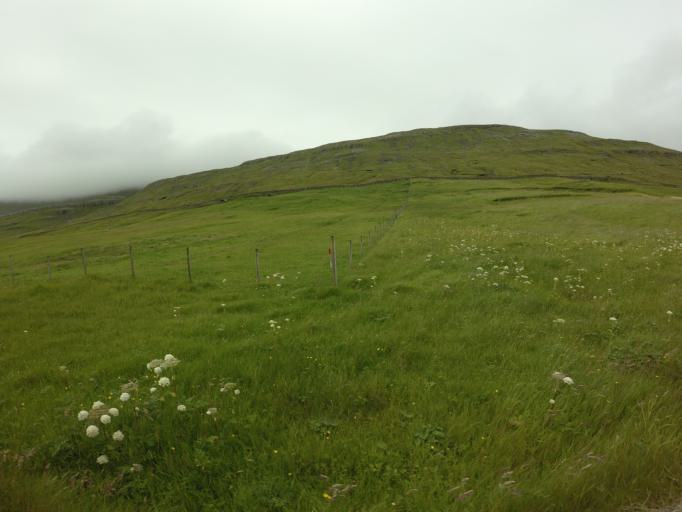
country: FO
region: Sandoy
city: Sandur
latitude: 61.8120
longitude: -6.6906
